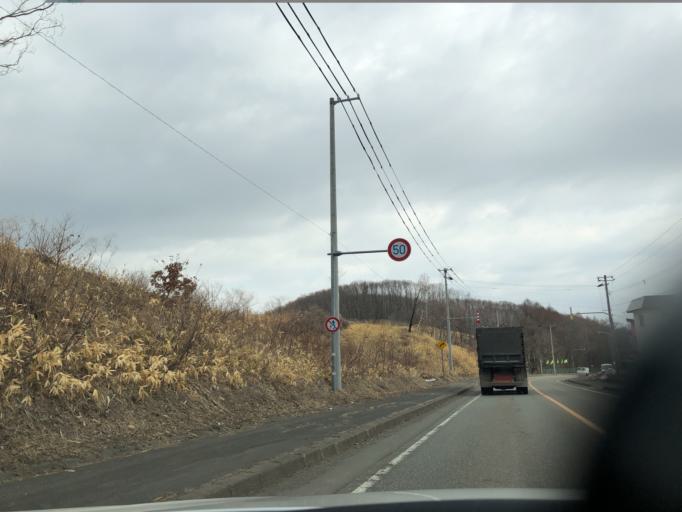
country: JP
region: Hokkaido
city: Chitose
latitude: 42.7625
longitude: 141.8030
